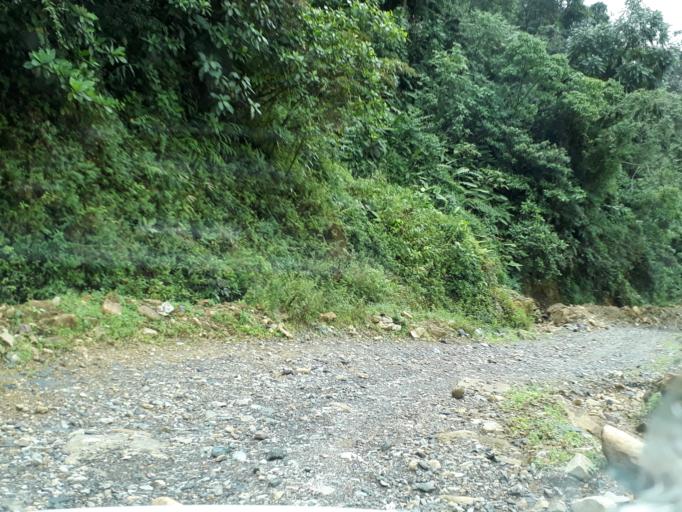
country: CO
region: Cundinamarca
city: Gachala
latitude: 4.7095
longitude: -73.3717
